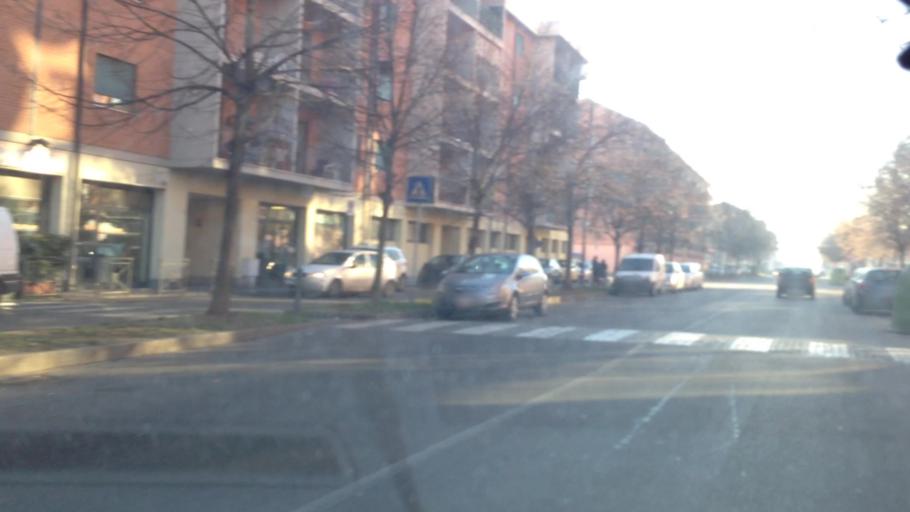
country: IT
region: Piedmont
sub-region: Provincia di Asti
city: Asti
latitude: 44.8933
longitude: 8.2184
